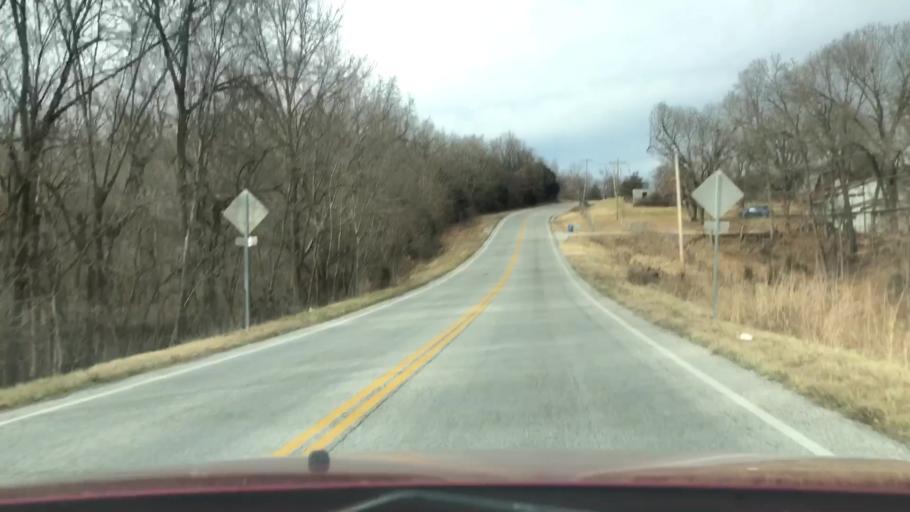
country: US
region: Missouri
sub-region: Greene County
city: Springfield
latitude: 37.2814
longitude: -93.2637
